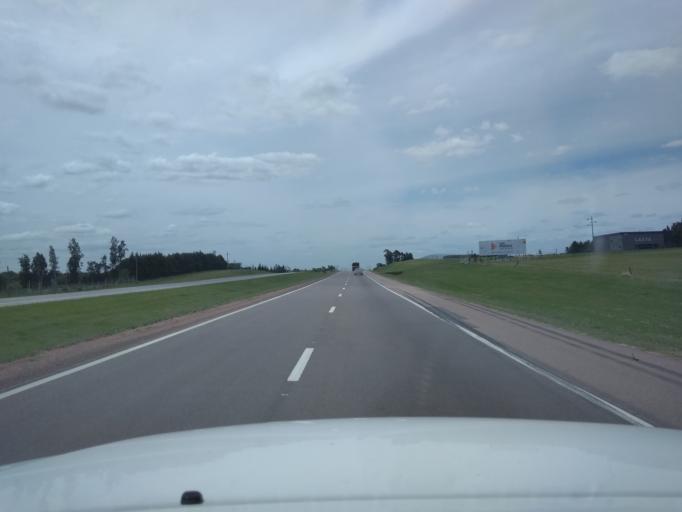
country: UY
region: Canelones
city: Las Piedras
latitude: -34.7351
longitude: -56.2498
